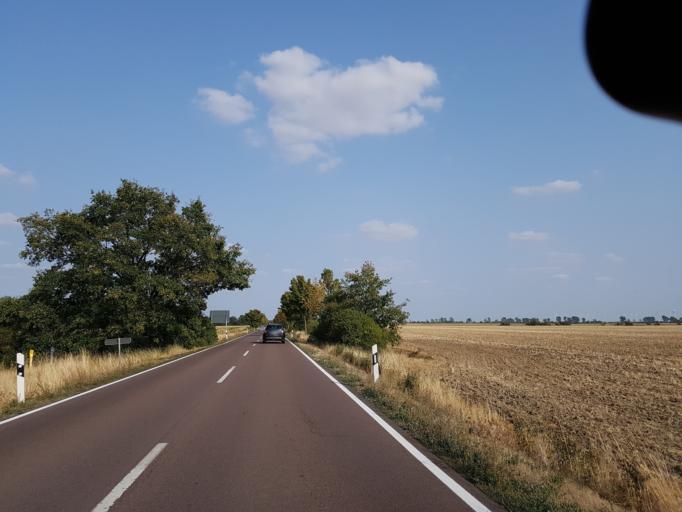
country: DE
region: Saxony-Anhalt
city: Kemberg
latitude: 51.8068
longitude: 12.6527
